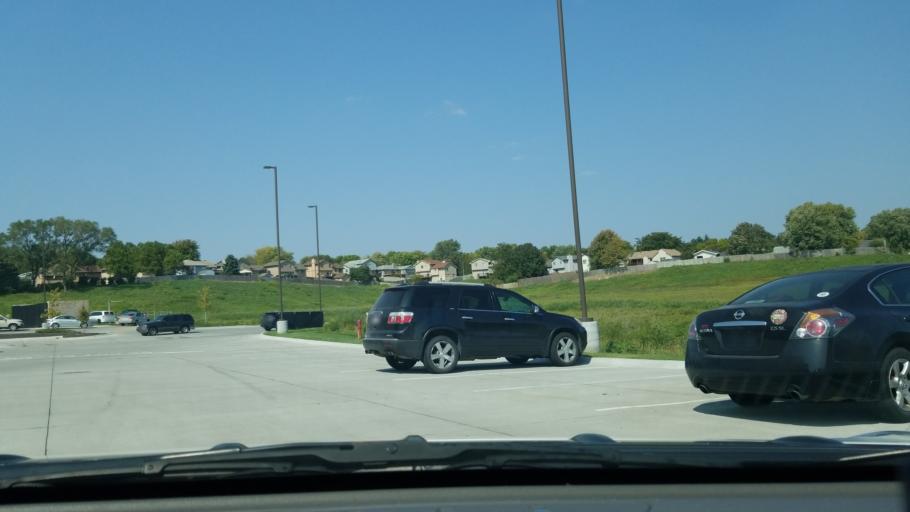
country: US
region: Nebraska
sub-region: Sarpy County
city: Offutt Air Force Base
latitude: 41.1584
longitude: -95.9290
